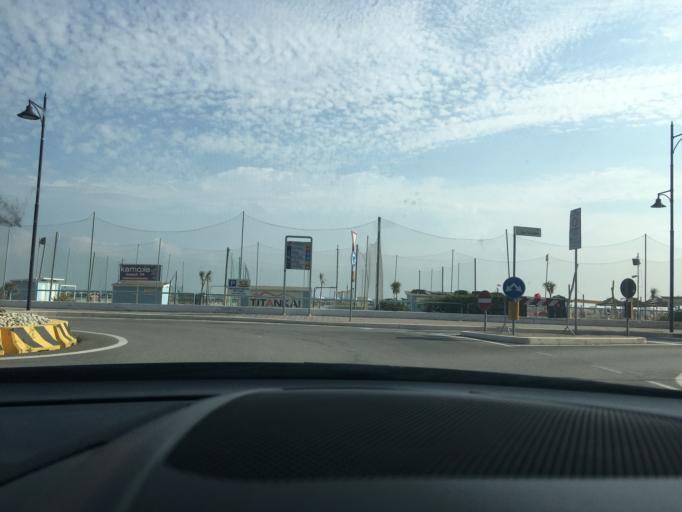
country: IT
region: Emilia-Romagna
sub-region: Provincia di Rimini
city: Bellaria-Igea Marina
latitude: 44.1135
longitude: 12.5046
